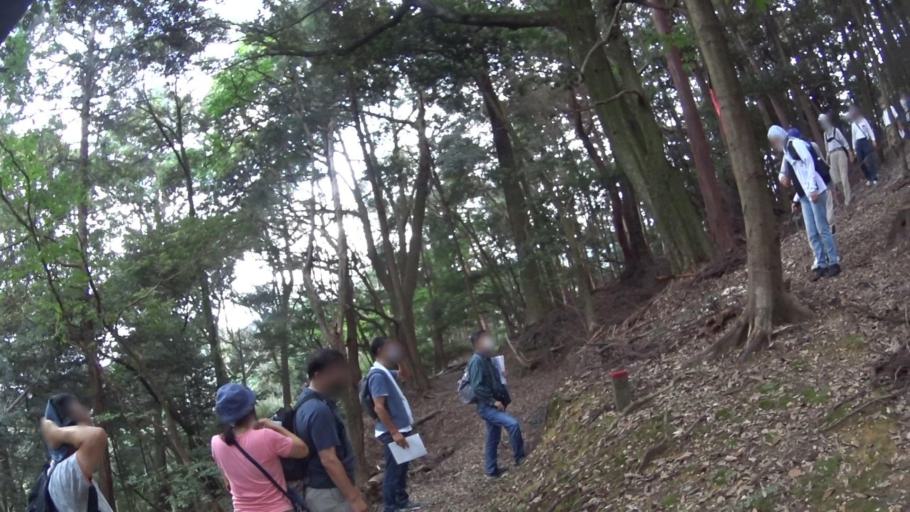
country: JP
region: Shiga Prefecture
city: Hikone
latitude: 35.2830
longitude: 136.3992
